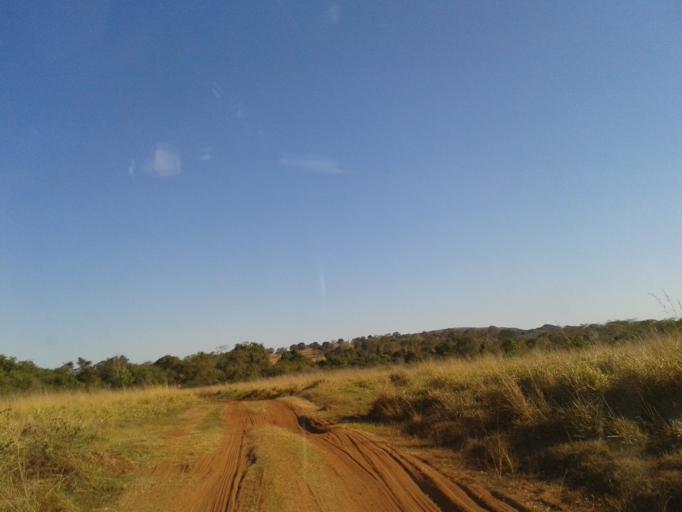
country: BR
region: Minas Gerais
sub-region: Santa Vitoria
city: Santa Vitoria
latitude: -19.1630
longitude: -50.0211
